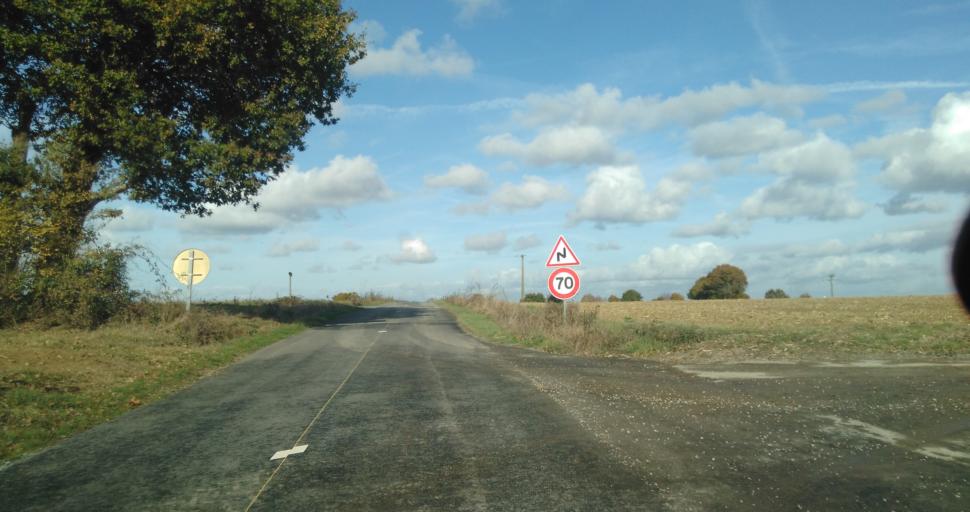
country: FR
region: Brittany
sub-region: Departement d'Ille-et-Vilaine
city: Boisgervilly
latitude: 48.1190
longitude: -2.0873
